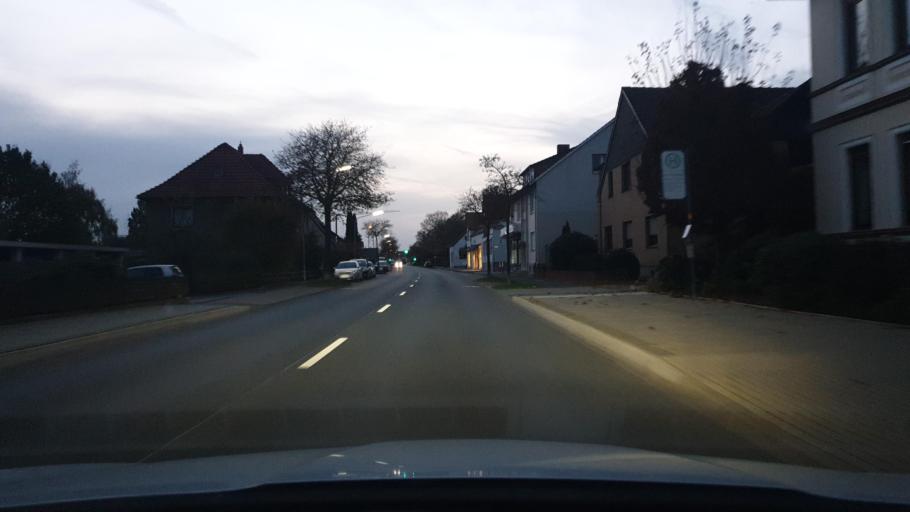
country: DE
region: North Rhine-Westphalia
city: Spenge
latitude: 52.0977
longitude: 8.5099
